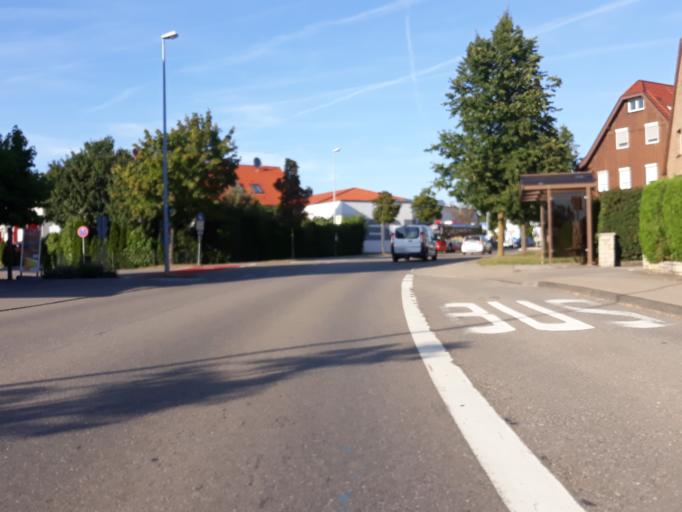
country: DE
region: Baden-Wuerttemberg
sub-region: Regierungsbezirk Stuttgart
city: Altdorf
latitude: 48.6325
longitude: 8.9976
